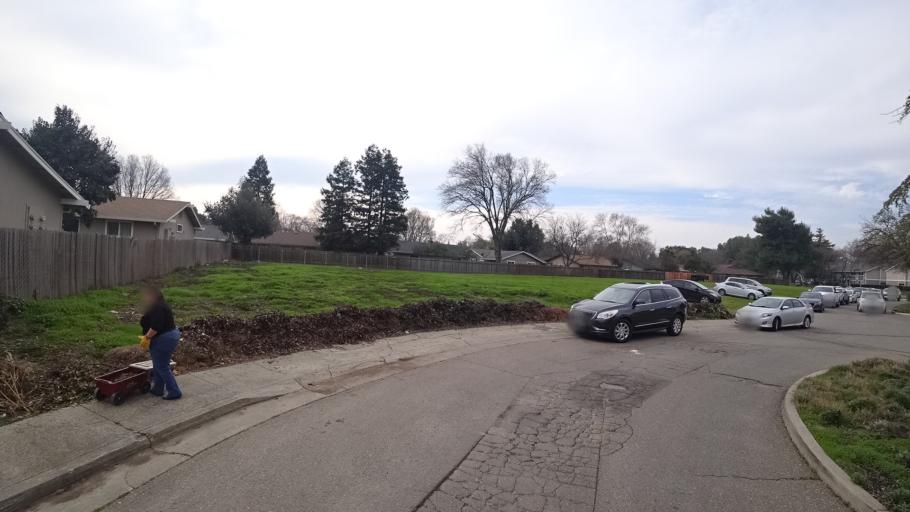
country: US
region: California
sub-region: Yolo County
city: Davis
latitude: 38.5594
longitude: -121.7375
